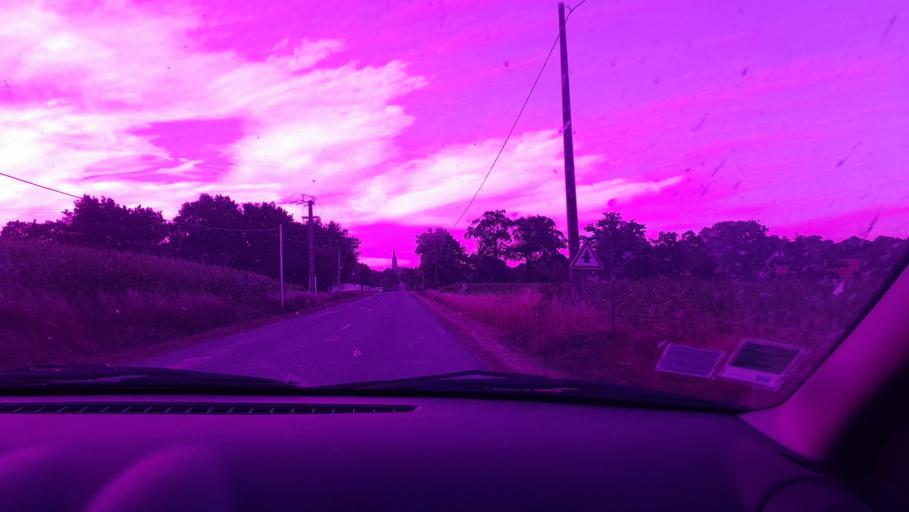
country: FR
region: Brittany
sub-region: Departement d'Ille-et-Vilaine
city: Le Pertre
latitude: 48.0195
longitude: -1.0377
